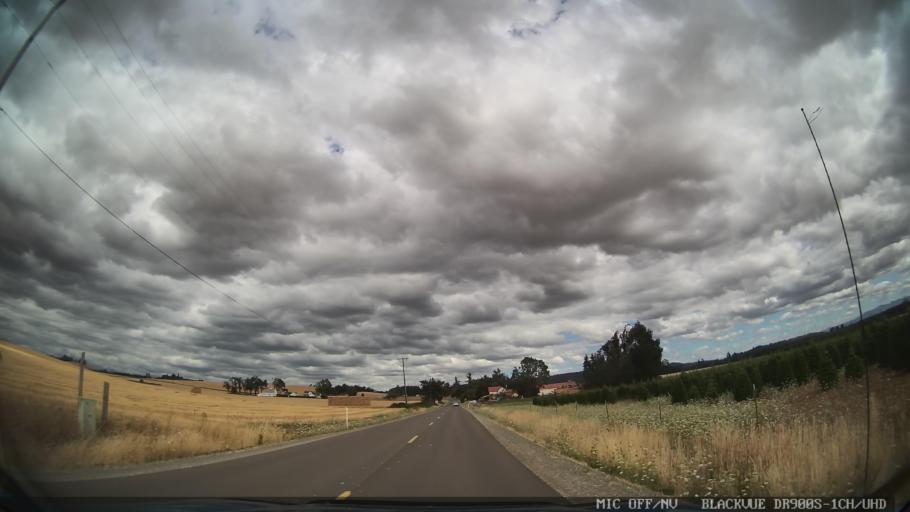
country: US
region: Oregon
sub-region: Marion County
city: Sublimity
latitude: 44.8661
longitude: -122.7618
